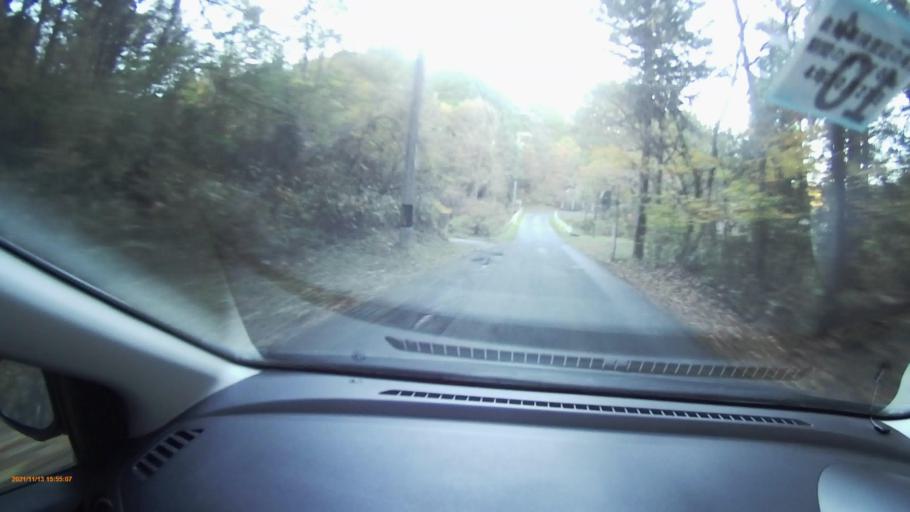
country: JP
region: Gifu
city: Nakatsugawa
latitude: 35.5963
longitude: 137.4485
